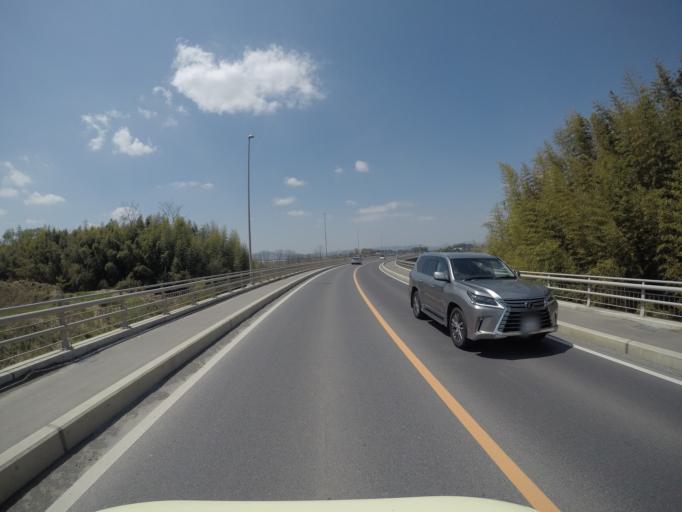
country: JP
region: Tochigi
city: Mibu
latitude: 36.3901
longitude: 139.7963
